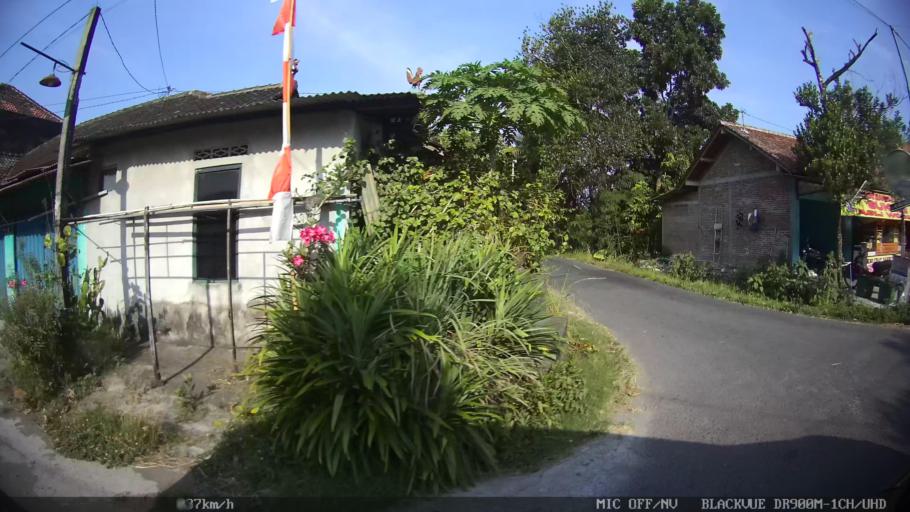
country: ID
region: Daerah Istimewa Yogyakarta
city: Bantul
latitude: -7.8878
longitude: 110.3039
